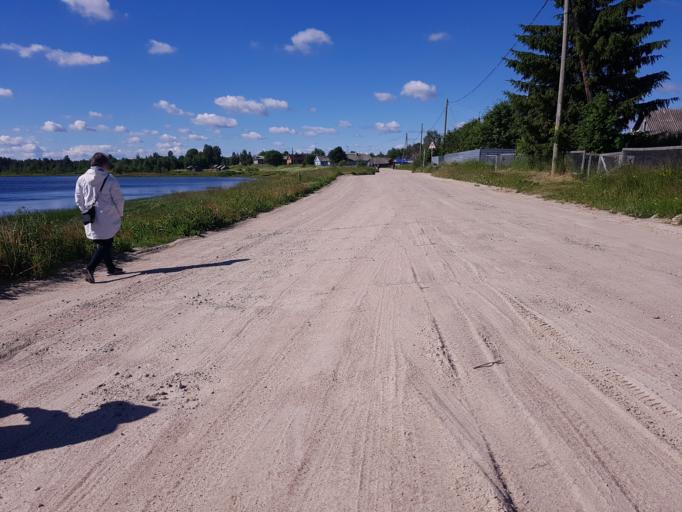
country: RU
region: Republic of Karelia
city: Yushkozero
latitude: 64.7514
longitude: 32.1100
